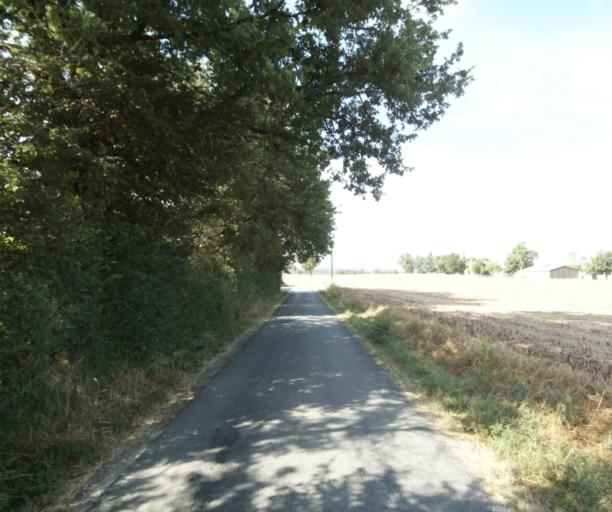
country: FR
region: Midi-Pyrenees
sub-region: Departement du Tarn
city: Soreze
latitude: 43.5003
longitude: 2.0470
